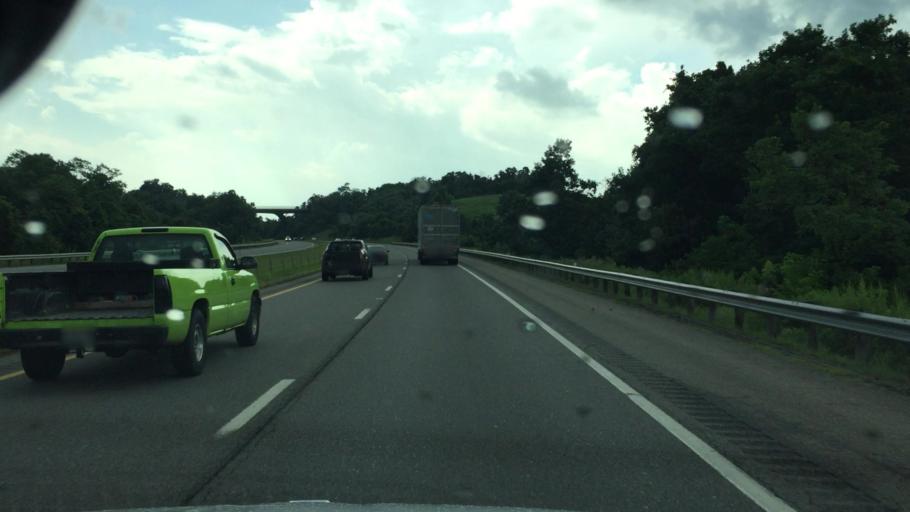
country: US
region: Ohio
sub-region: Belmont County
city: Wolfhurst
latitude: 40.0572
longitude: -80.8223
